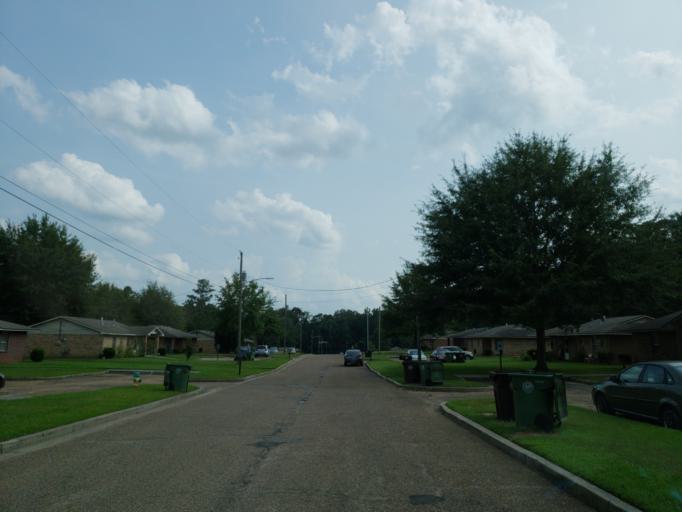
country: US
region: Mississippi
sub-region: Forrest County
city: Hattiesburg
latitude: 31.2984
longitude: -89.3264
